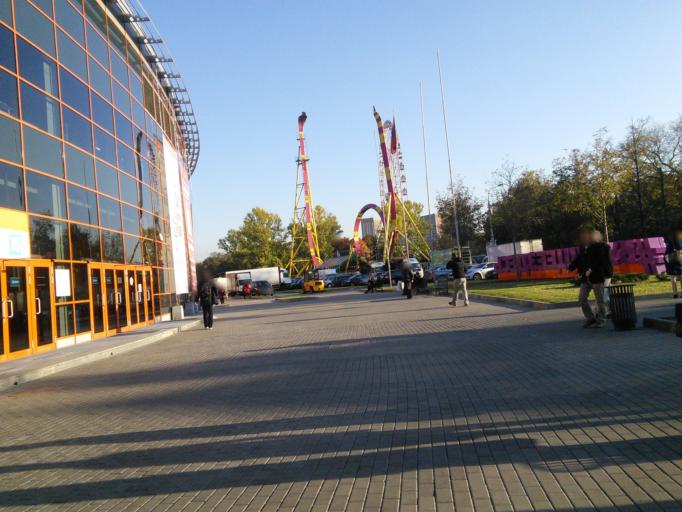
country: RU
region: Moscow
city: Sviblovo
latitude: 55.8299
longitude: 37.6379
